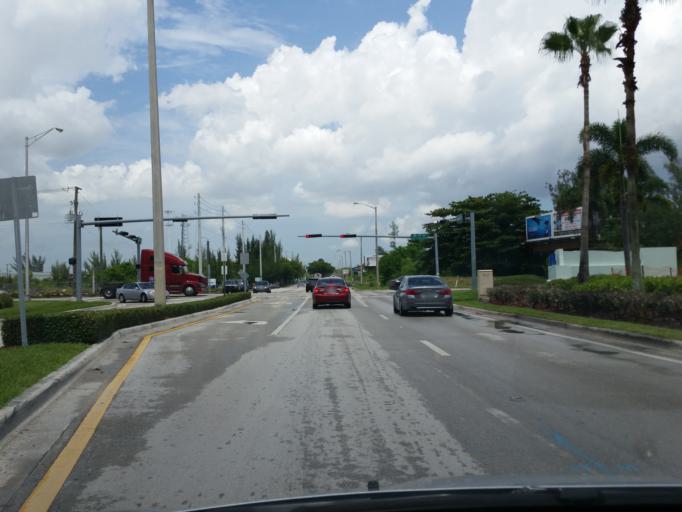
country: US
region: Florida
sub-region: Miami-Dade County
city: Sweetwater
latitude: 25.7861
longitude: -80.3760
